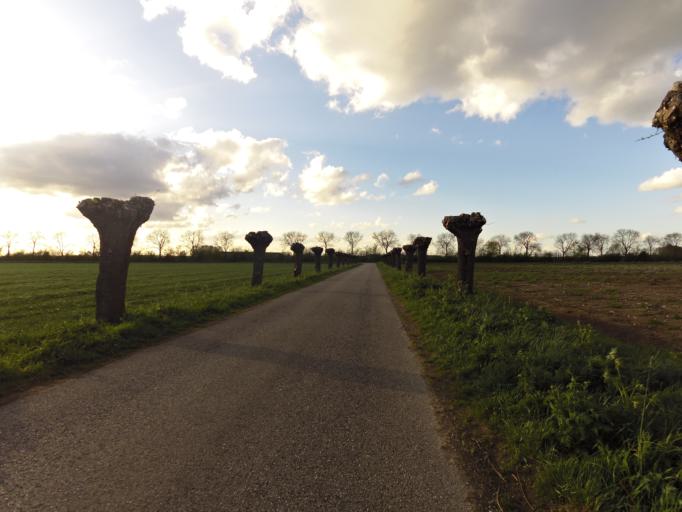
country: NL
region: Gelderland
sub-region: Gemeente Doesburg
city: Doesburg
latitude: 51.9689
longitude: 6.1181
